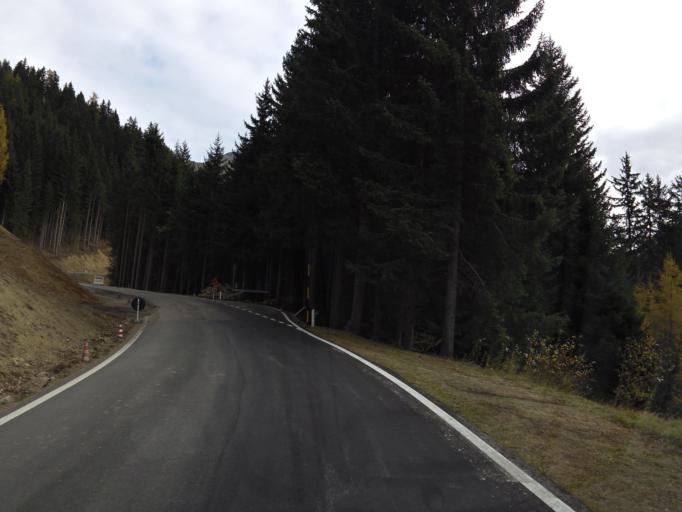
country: IT
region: Trentino-Alto Adige
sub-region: Bolzano
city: Racines
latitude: 46.8297
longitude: 11.2991
